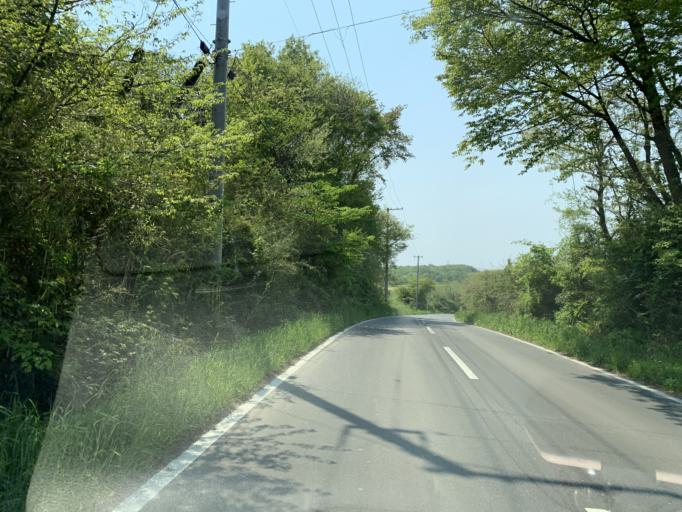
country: JP
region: Iwate
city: Ichinoseki
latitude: 38.8520
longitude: 141.0556
